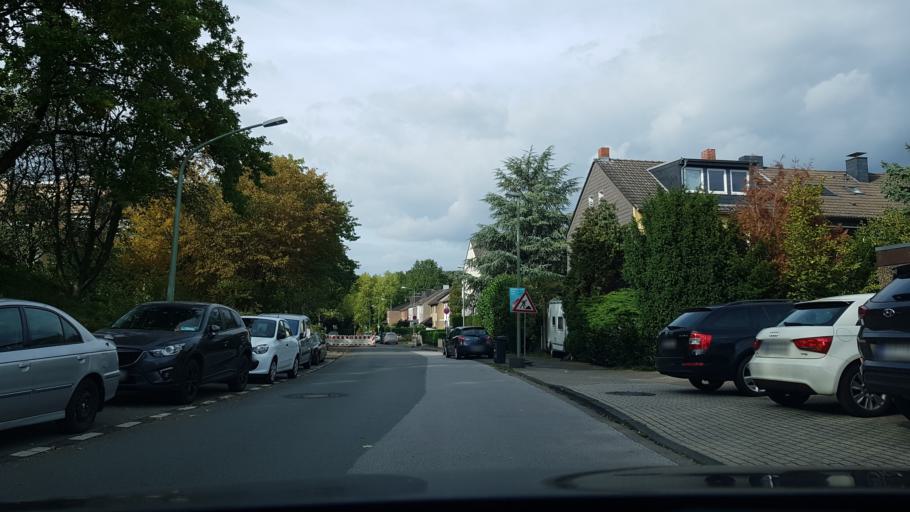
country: DE
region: North Rhine-Westphalia
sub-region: Regierungsbezirk Dusseldorf
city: Hochfeld
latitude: 51.3727
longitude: 6.7849
